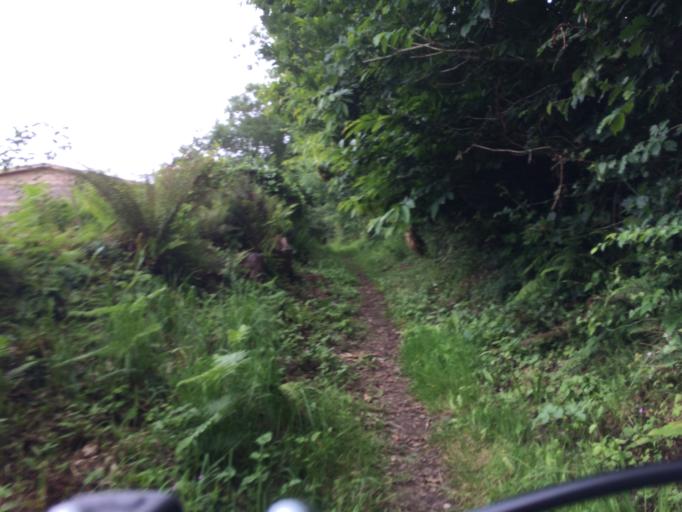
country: FR
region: Brittany
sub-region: Departement du Finistere
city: Hopital-Camfrout
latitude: 48.3295
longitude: -4.2514
